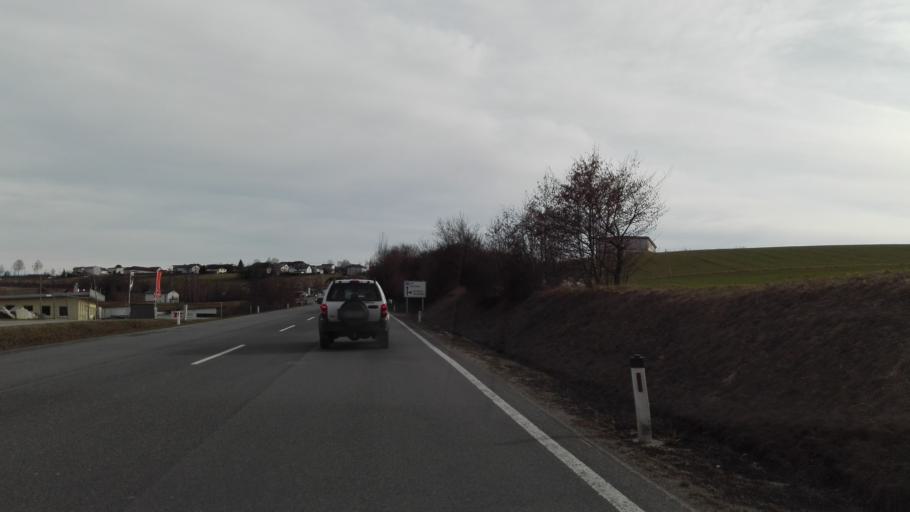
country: AT
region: Upper Austria
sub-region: Politischer Bezirk Rohrbach
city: Kleinzell im Muehlkreis
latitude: 48.4936
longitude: 13.9703
